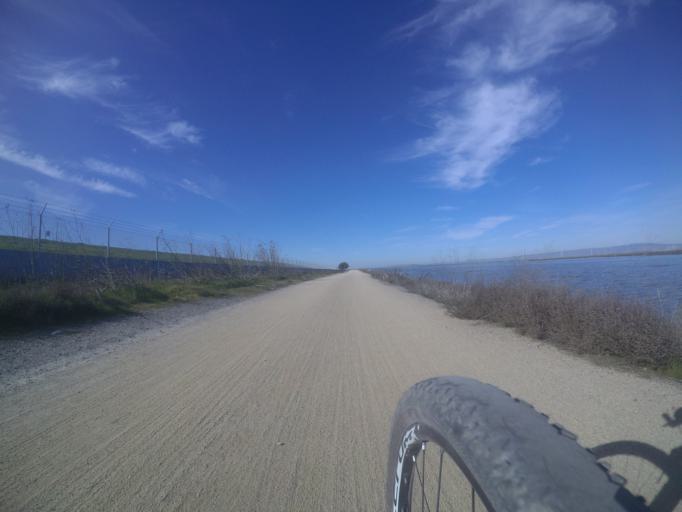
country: US
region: California
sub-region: Santa Clara County
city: Mountain View
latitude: 37.4317
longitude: -122.0518
